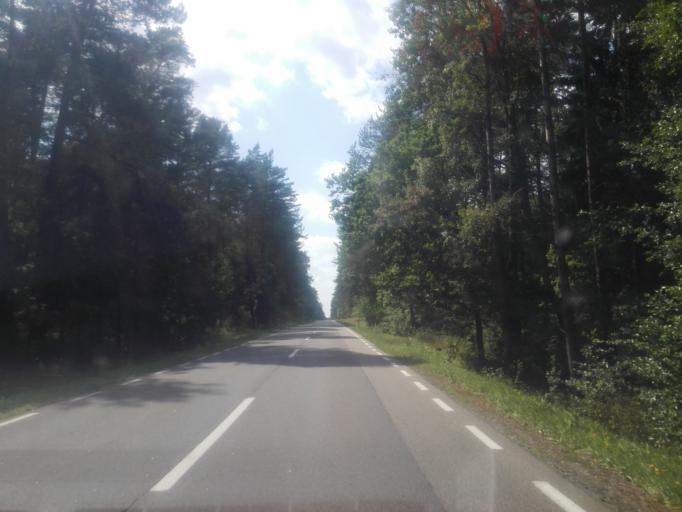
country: PL
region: Podlasie
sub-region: Powiat augustowski
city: Augustow
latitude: 53.8471
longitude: 23.0280
